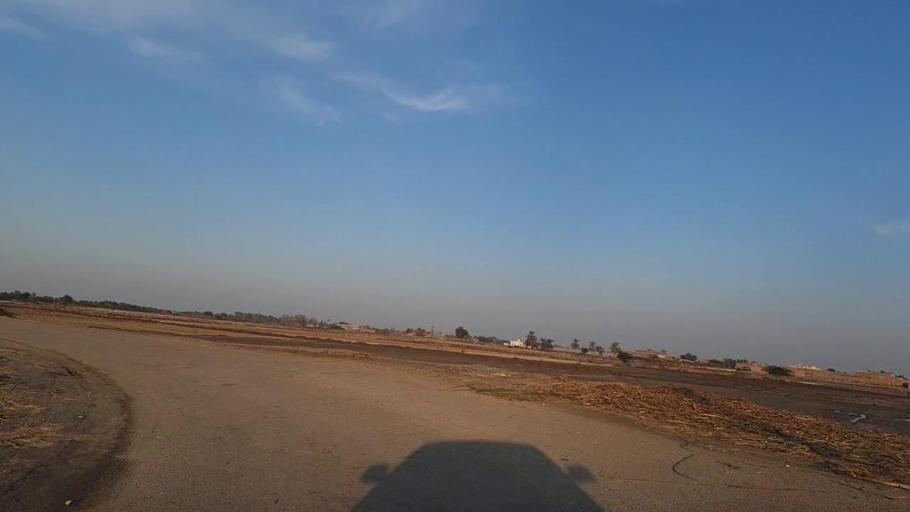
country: PK
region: Sindh
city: Bandhi
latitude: 26.5884
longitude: 68.3408
